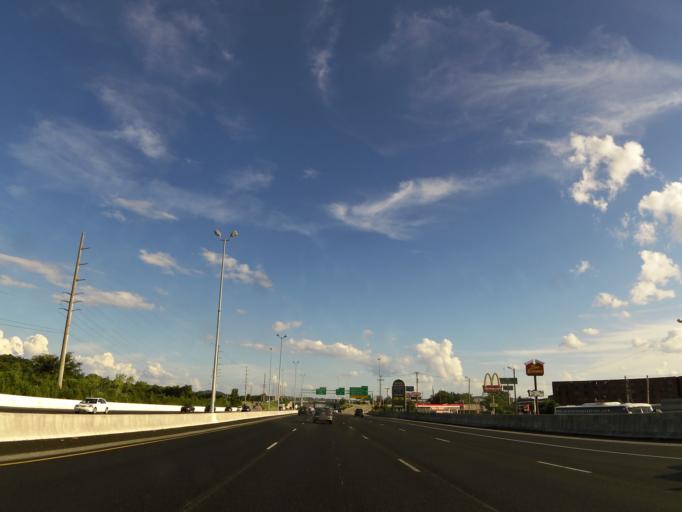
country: US
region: Tennessee
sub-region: Davidson County
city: Lakewood
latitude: 36.2216
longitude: -86.6935
